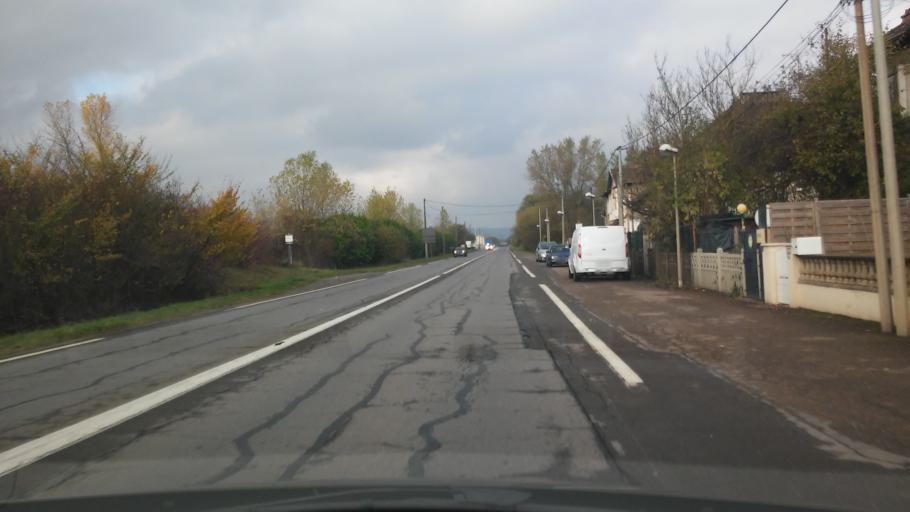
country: FR
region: Lorraine
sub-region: Departement de la Moselle
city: Uckange
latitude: 49.3155
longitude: 6.1572
